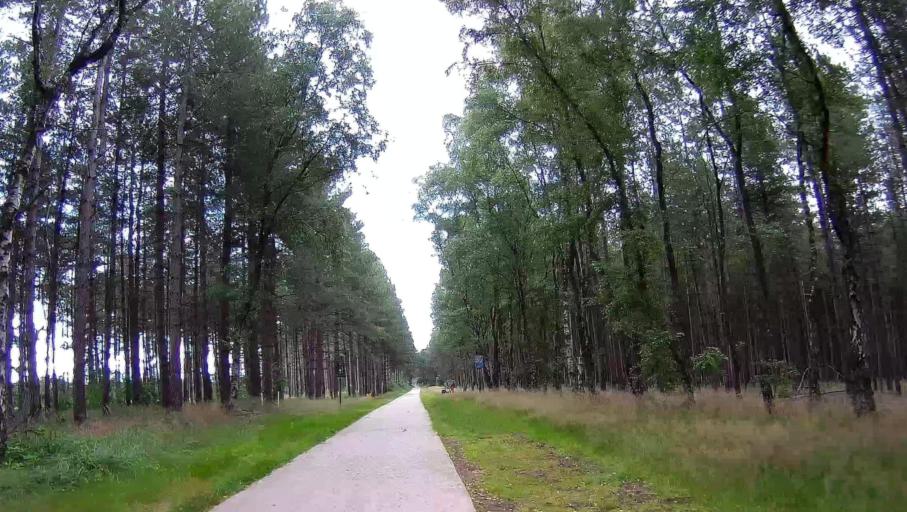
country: BE
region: Flanders
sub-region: Provincie Limburg
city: Lommel
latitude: 51.2466
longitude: 5.2846
